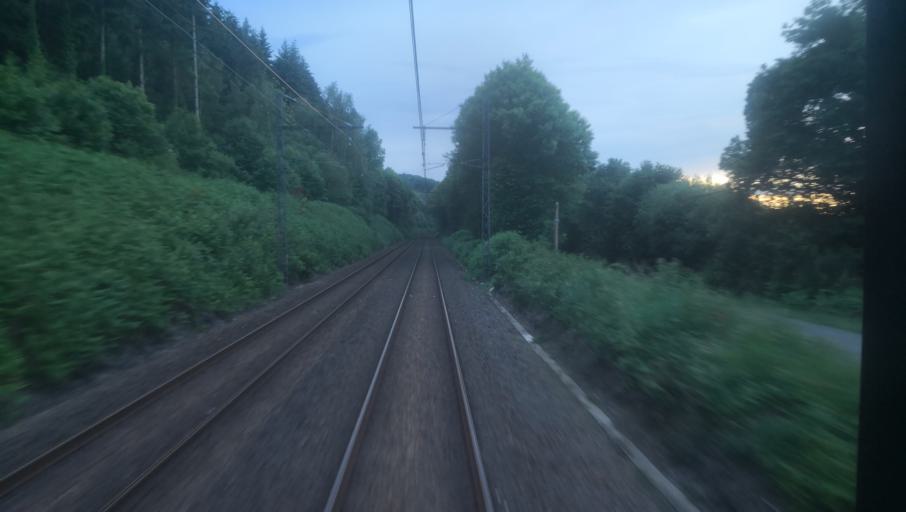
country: FR
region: Limousin
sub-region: Departement de la Haute-Vienne
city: Bessines-sur-Gartempe
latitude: 46.0549
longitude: 1.4606
